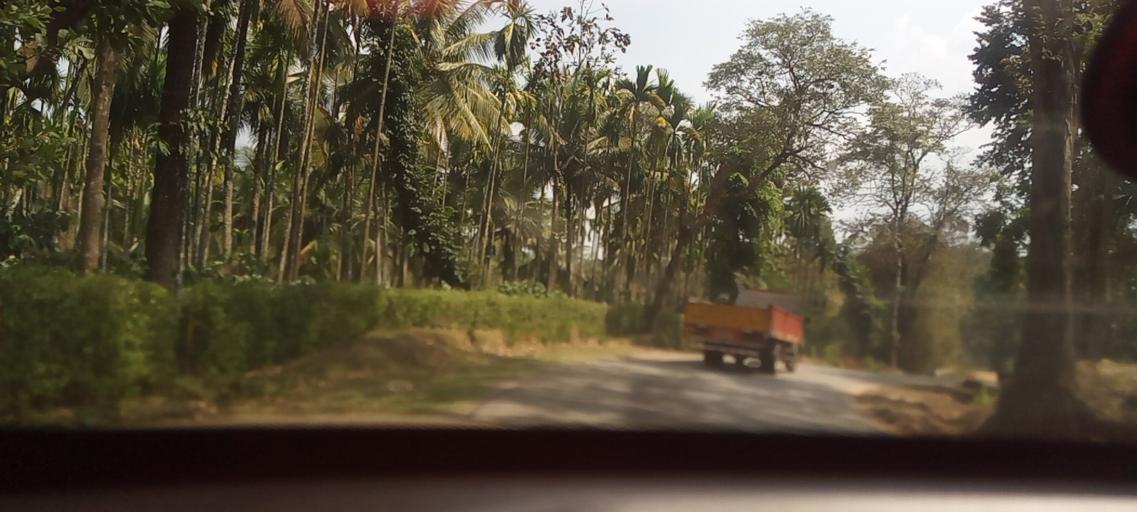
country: IN
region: Karnataka
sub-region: Chikmagalur
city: Mudigere
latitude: 13.3243
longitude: 75.5625
